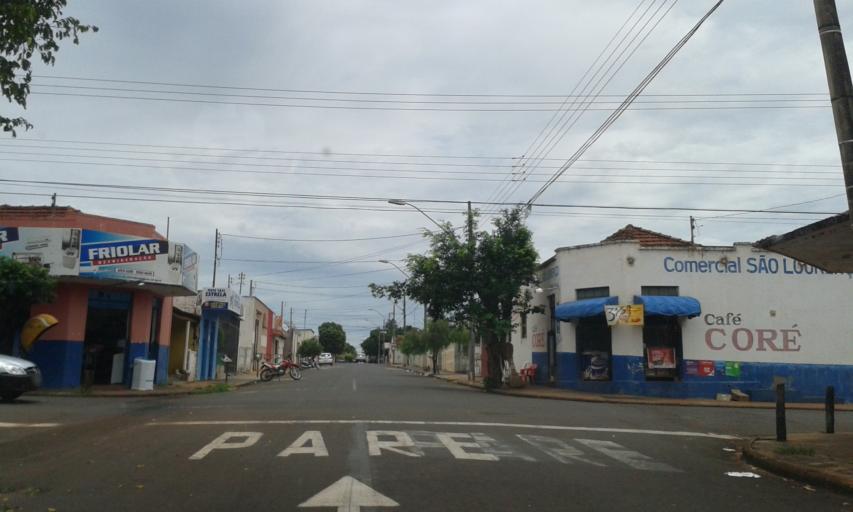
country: BR
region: Minas Gerais
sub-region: Ituiutaba
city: Ituiutaba
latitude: -18.9790
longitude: -49.4531
